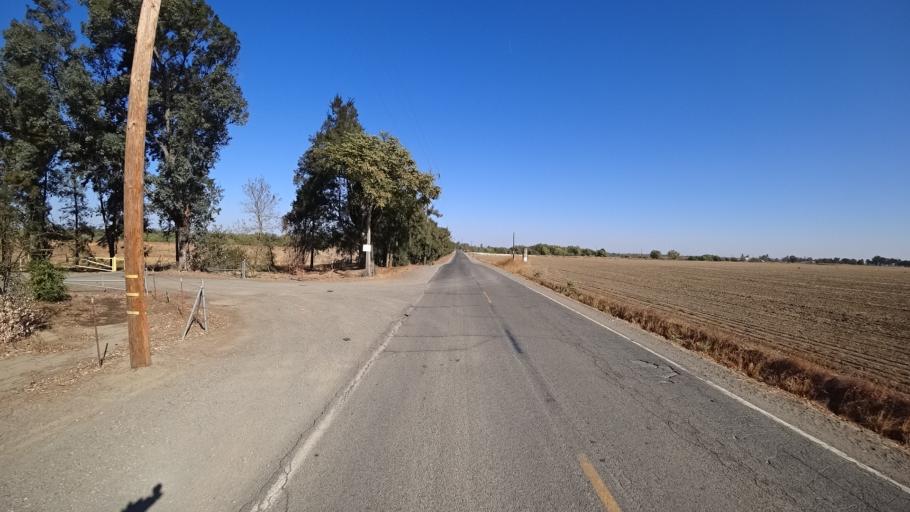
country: US
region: California
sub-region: Yolo County
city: Woodland
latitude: 38.6842
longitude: -121.8671
